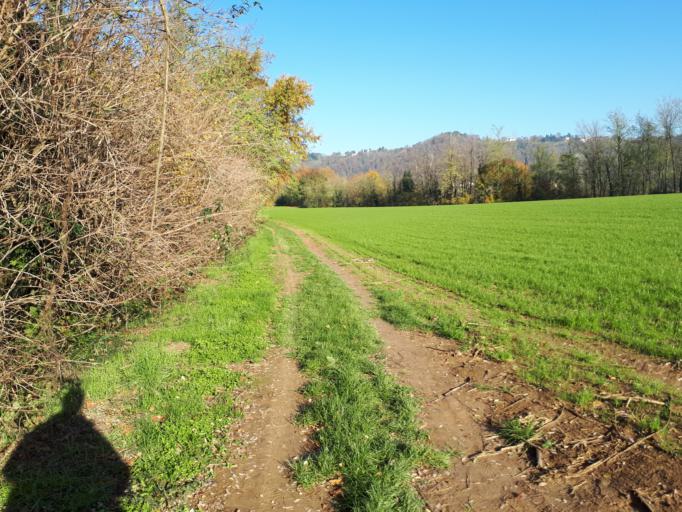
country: IT
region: Lombardy
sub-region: Provincia di Lecco
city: Maresso
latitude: 45.6946
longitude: 9.3613
